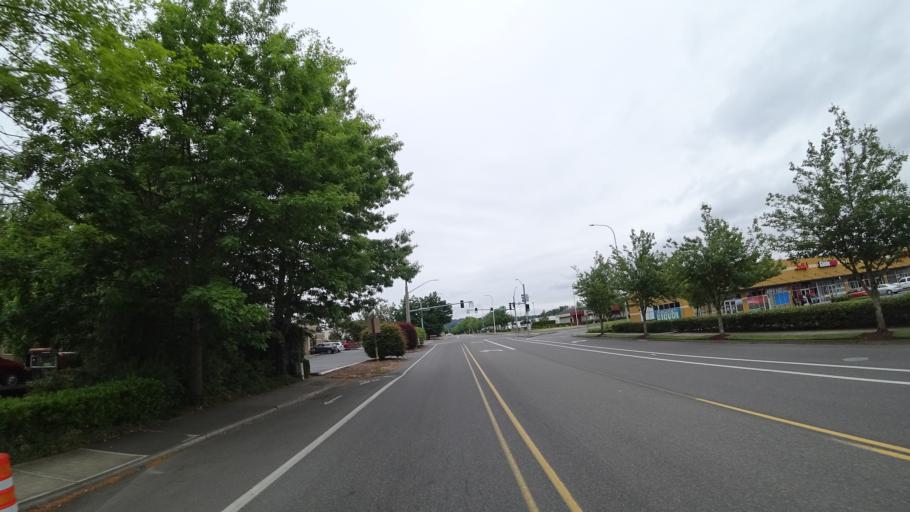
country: US
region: Oregon
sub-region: Multnomah County
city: Wood Village
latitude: 45.5428
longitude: -122.4192
